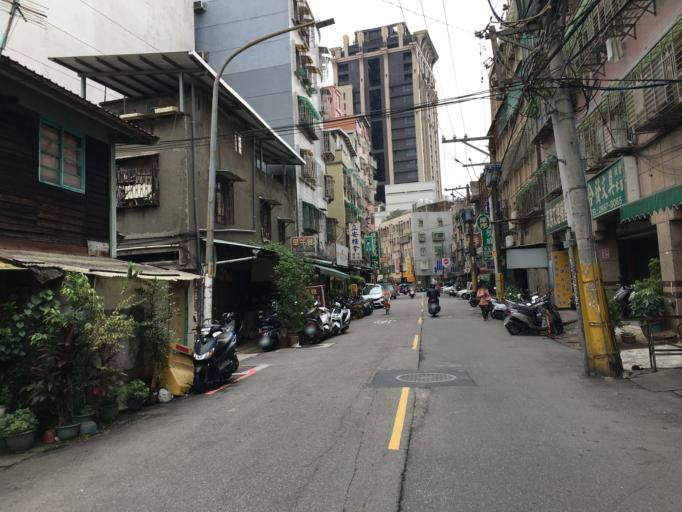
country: TW
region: Taipei
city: Taipei
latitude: 25.0658
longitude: 121.4942
